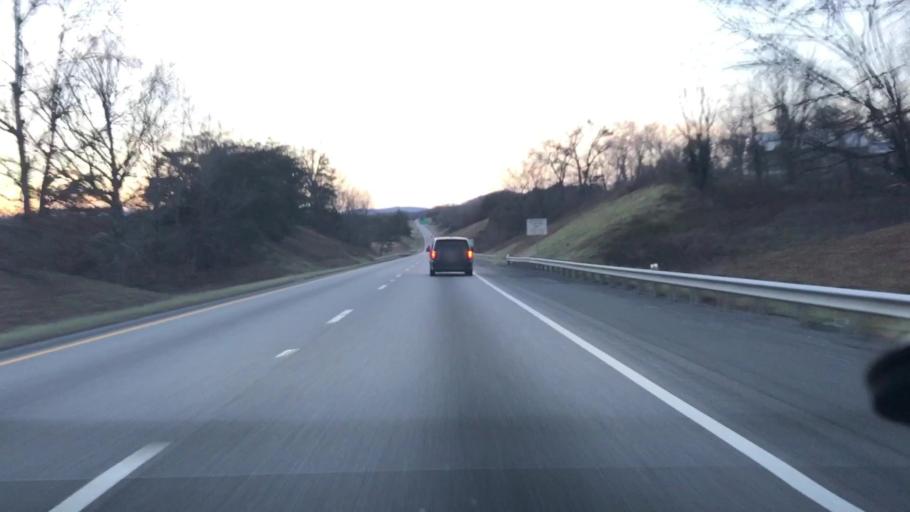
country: US
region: Virginia
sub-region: Augusta County
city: Fishersville
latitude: 38.1069
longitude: -79.0162
